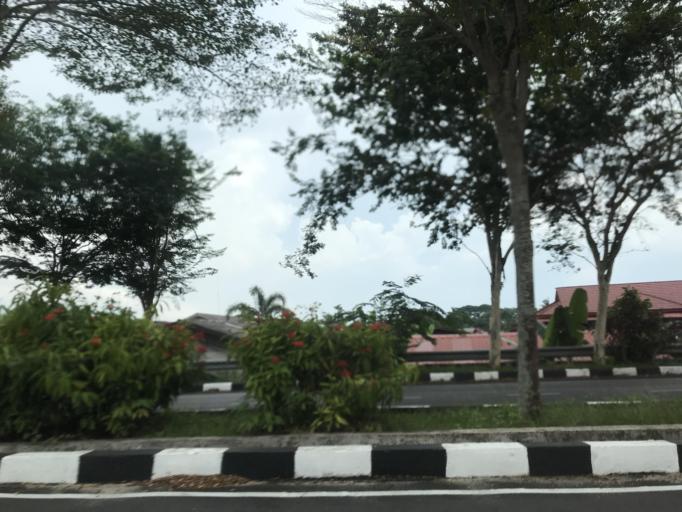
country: MY
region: Kelantan
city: Kota Bharu
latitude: 6.1108
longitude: 102.2342
